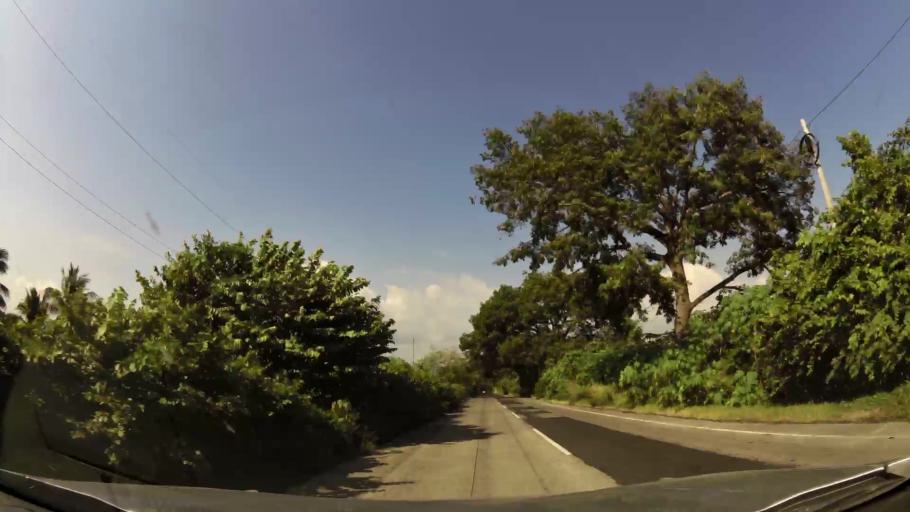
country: GT
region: Escuintla
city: Puerto San Jose
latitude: 13.9828
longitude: -90.7884
